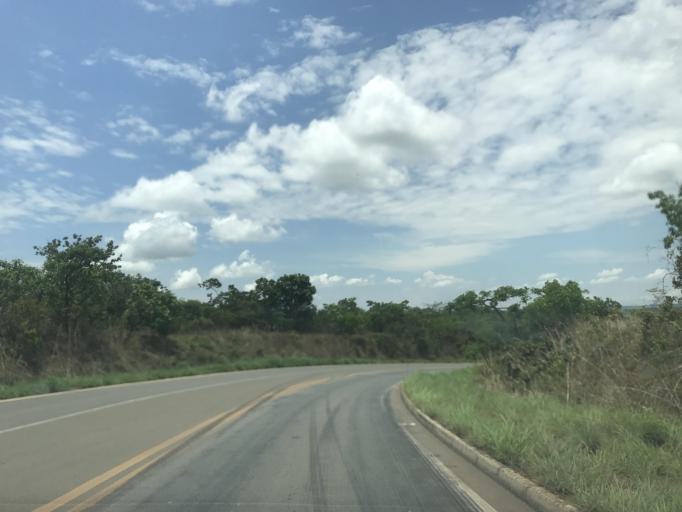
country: BR
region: Goias
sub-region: Luziania
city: Luziania
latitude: -16.3994
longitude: -48.1714
